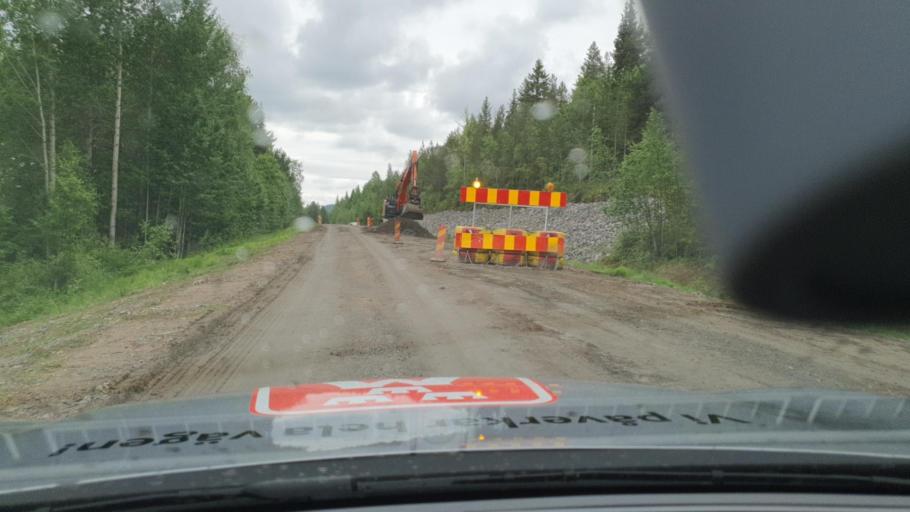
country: SE
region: Norrbotten
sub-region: Overtornea Kommun
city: OEvertornea
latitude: 66.4091
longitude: 23.6043
